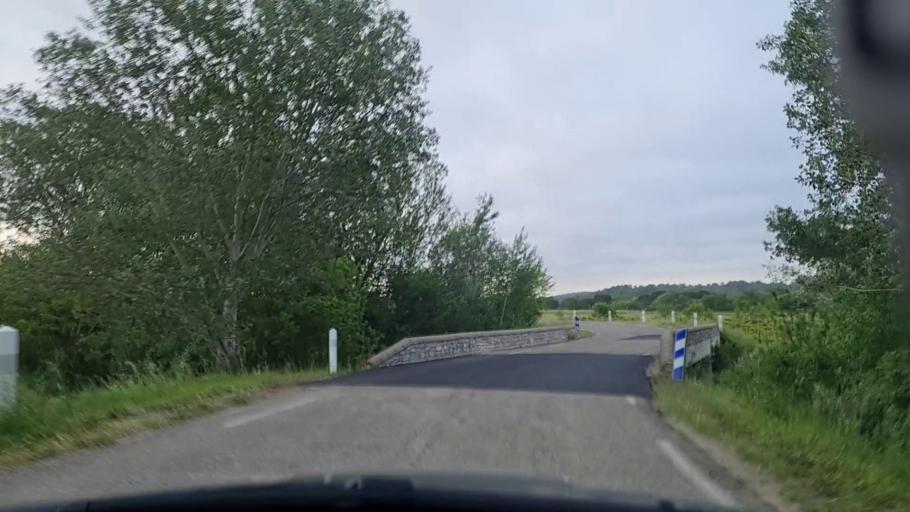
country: FR
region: Languedoc-Roussillon
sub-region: Departement du Gard
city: Villevieille
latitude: 43.8264
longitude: 4.1244
